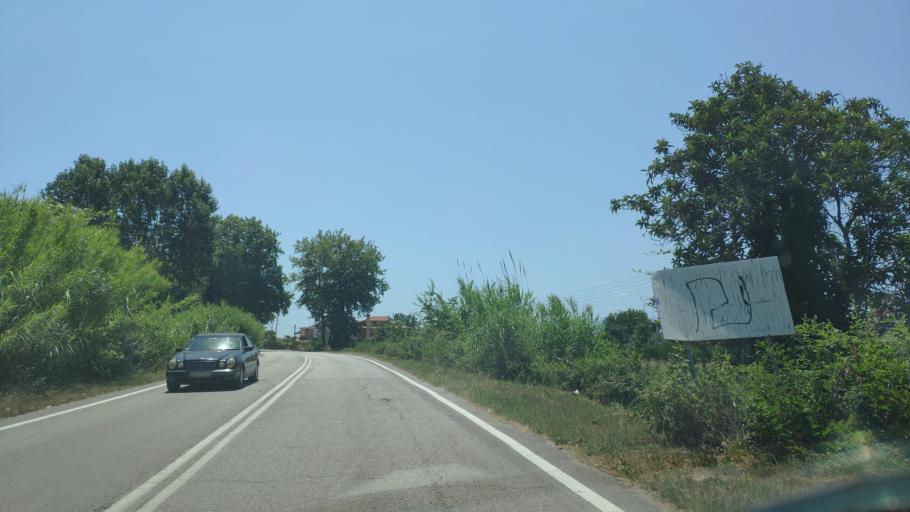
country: GR
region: Epirus
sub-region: Nomos Artas
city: Neochori
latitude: 39.0877
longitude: 21.0149
